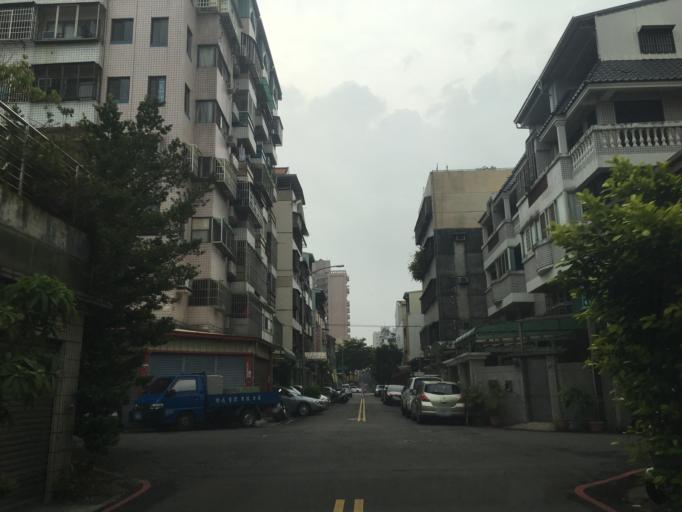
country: TW
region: Taiwan
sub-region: Taichung City
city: Taichung
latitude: 24.1759
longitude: 120.6792
